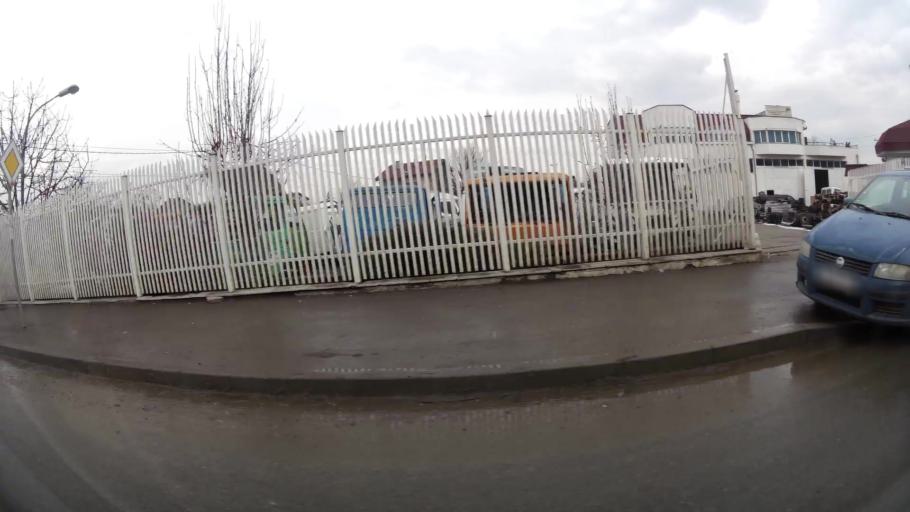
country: BG
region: Sofiya
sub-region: Obshtina Bozhurishte
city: Bozhurishte
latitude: 42.6960
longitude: 23.2289
